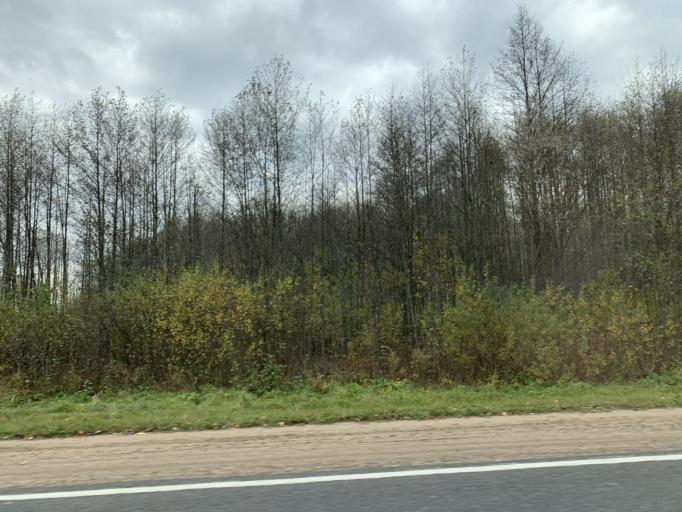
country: BY
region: Minsk
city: Stowbtsy
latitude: 53.5096
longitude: 26.7828
